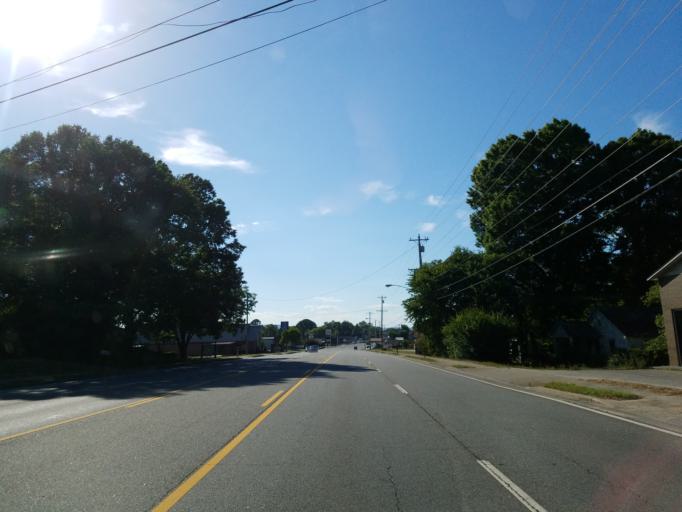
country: US
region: Georgia
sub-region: Gordon County
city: Calhoun
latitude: 34.4829
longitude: -84.9406
